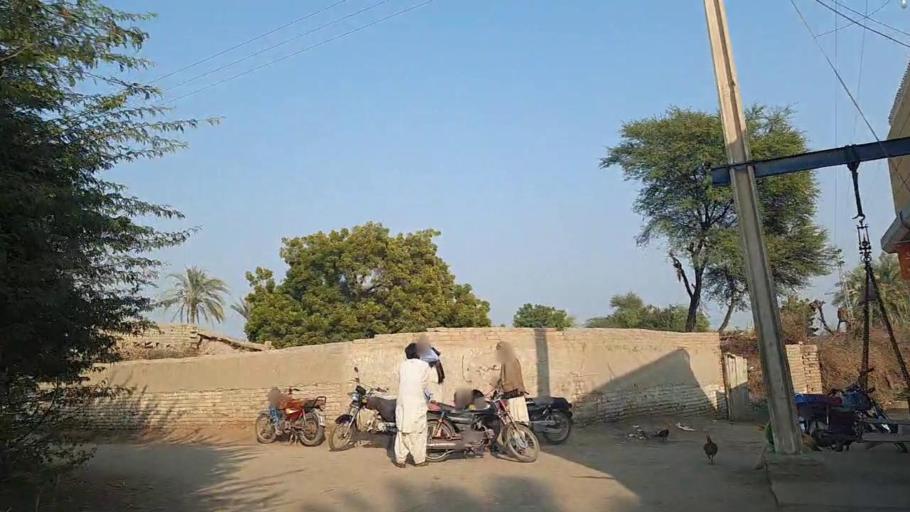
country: PK
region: Sindh
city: Jam Sahib
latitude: 26.2307
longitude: 68.5999
